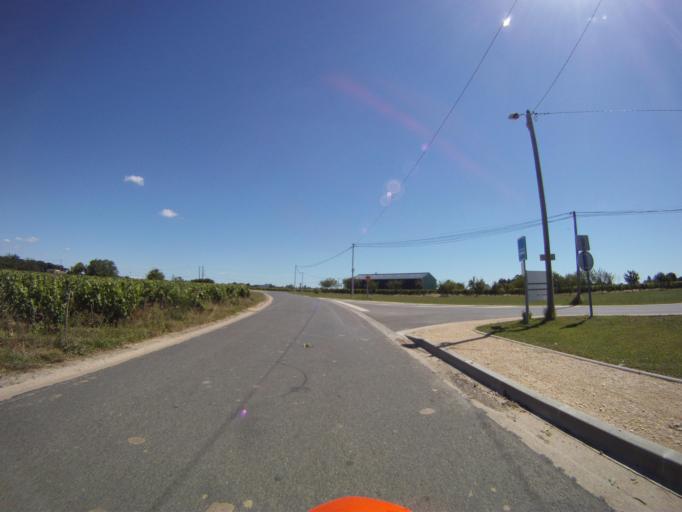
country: FR
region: Centre
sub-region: Departement d'Indre-et-Loire
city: Vouvray
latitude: 47.4549
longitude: 0.8005
